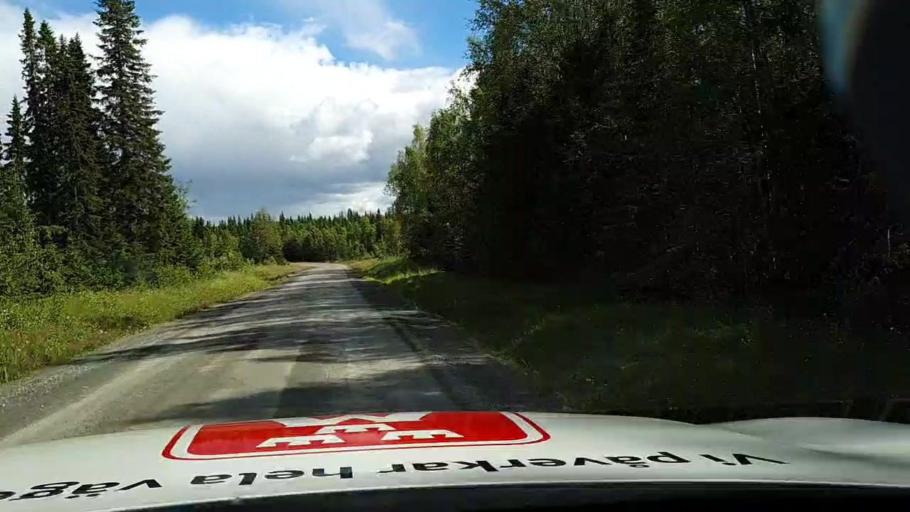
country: SE
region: Jaemtland
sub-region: Krokoms Kommun
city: Valla
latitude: 63.6584
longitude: 13.7616
